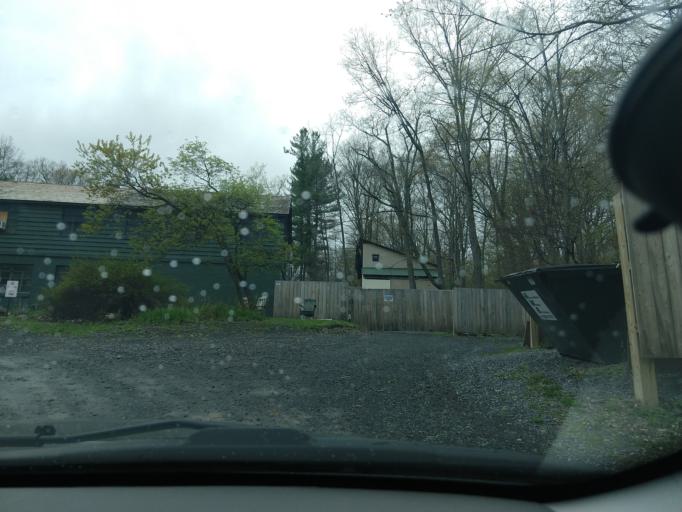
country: US
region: New York
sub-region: Tompkins County
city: Northwest Ithaca
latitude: 42.5187
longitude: -76.5570
